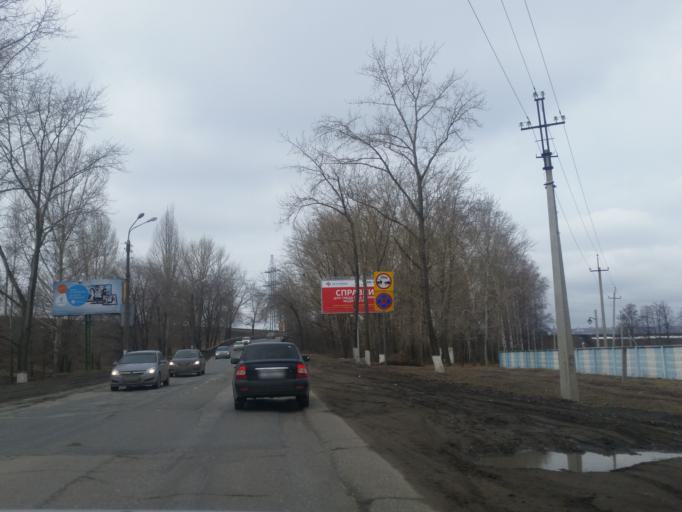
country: RU
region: Ulyanovsk
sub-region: Ulyanovskiy Rayon
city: Ulyanovsk
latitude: 54.3199
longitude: 48.4714
